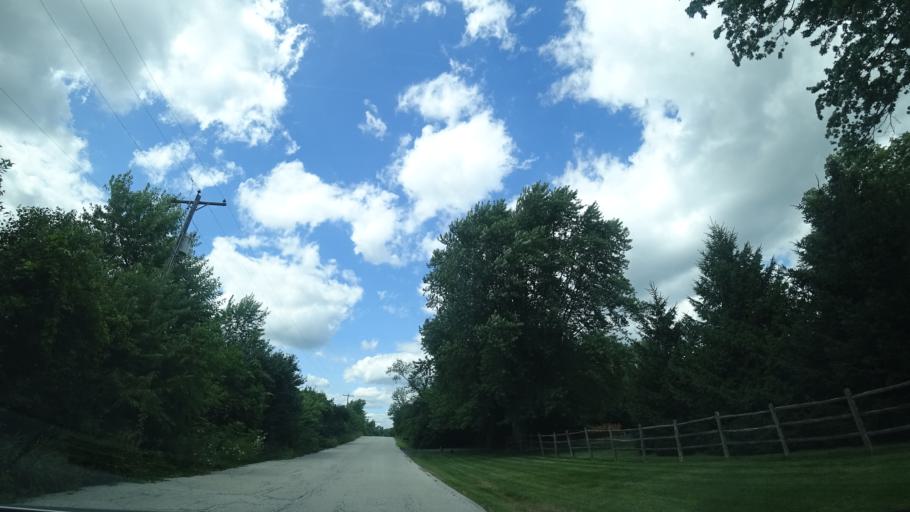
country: US
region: Illinois
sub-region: Will County
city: Homer Glen
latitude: 41.5938
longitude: -87.9057
